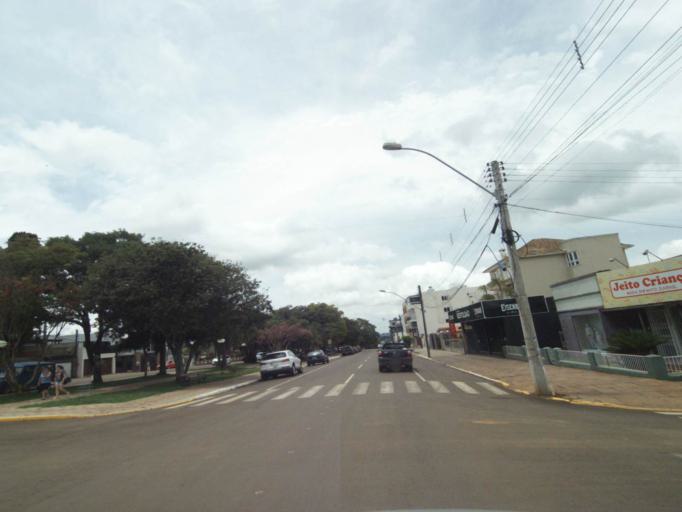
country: BR
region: Rio Grande do Sul
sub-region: Lagoa Vermelha
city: Lagoa Vermelha
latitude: -28.2117
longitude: -51.5198
